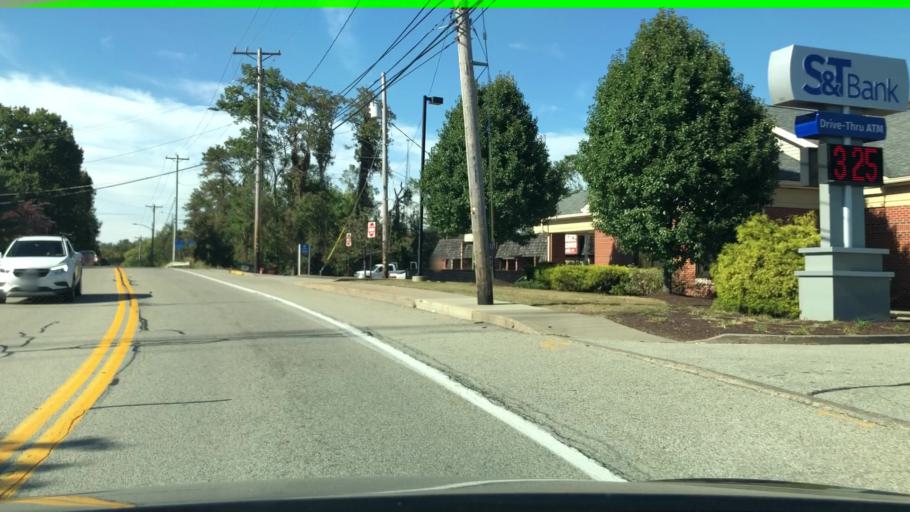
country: US
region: Pennsylvania
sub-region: Allegheny County
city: Penn Hills
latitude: 40.4726
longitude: -79.8197
